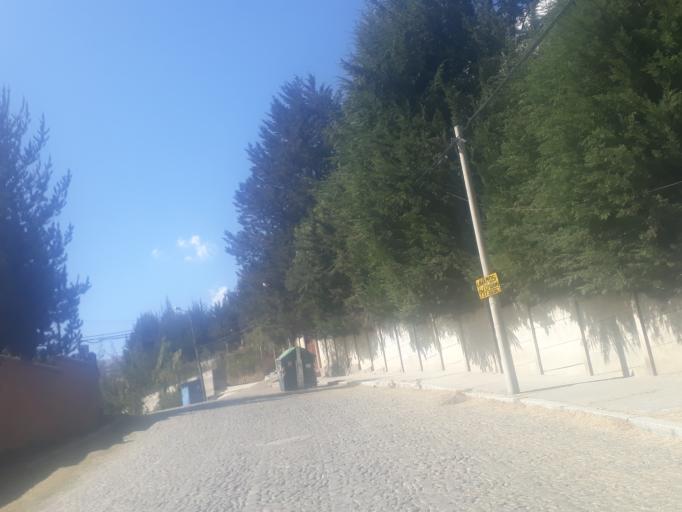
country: BO
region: La Paz
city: La Paz
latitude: -16.5382
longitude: -68.0559
